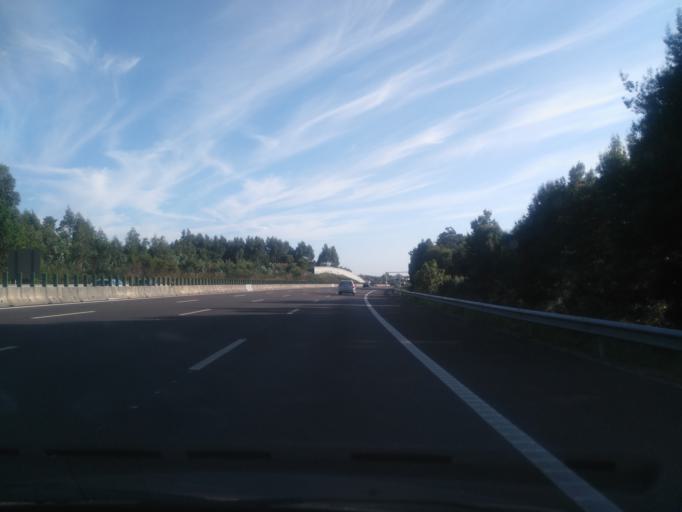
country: PT
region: Porto
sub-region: Vila Nova de Gaia
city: Grijo
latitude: 41.0394
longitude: -8.5702
